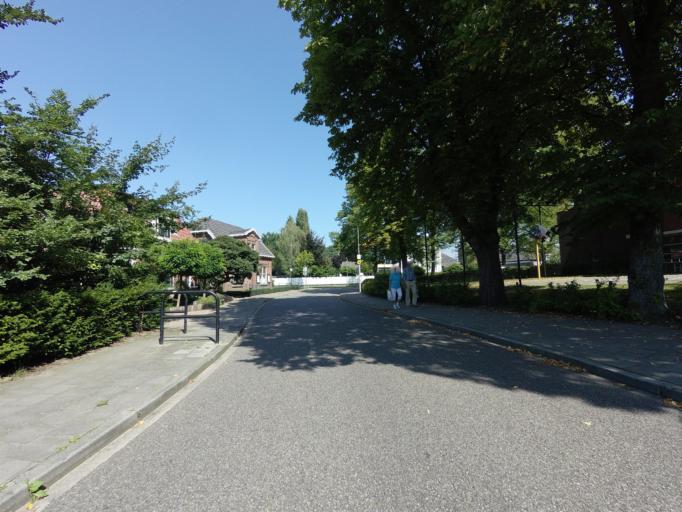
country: NL
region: Gelderland
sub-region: Berkelland
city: Neede
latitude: 52.1303
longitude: 6.6120
